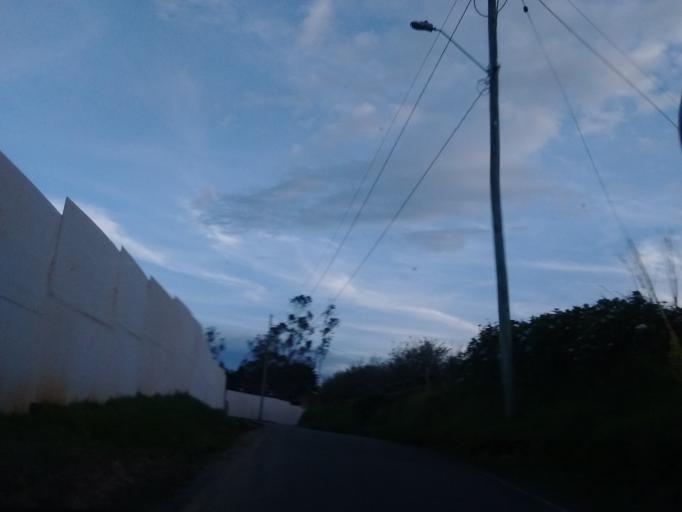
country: CO
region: Antioquia
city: Envigado
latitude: 6.1742
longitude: -75.5031
